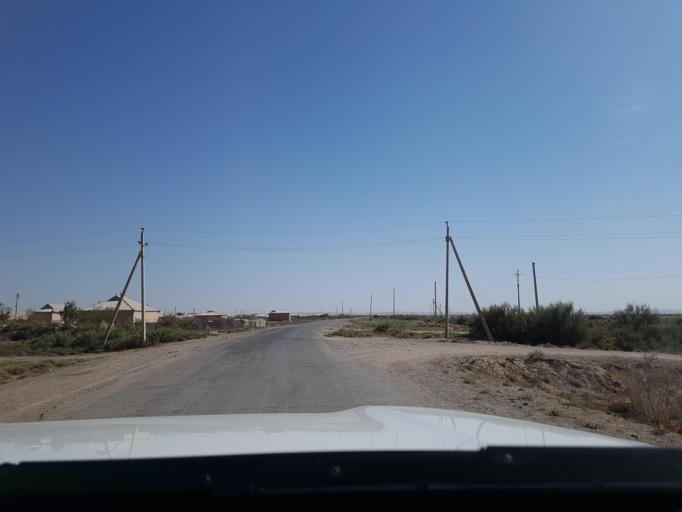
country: IR
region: Razavi Khorasan
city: Sarakhs
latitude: 36.5162
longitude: 61.2521
